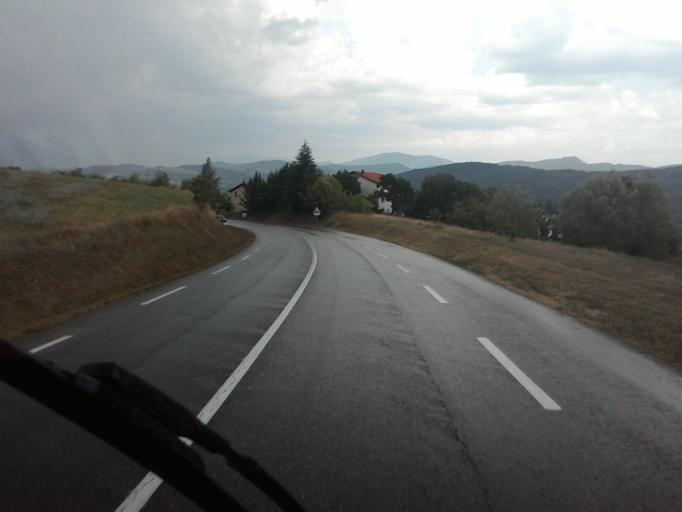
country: FR
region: Provence-Alpes-Cote d'Azur
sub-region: Departement des Hautes-Alpes
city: Gap
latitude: 44.5727
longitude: 6.0766
